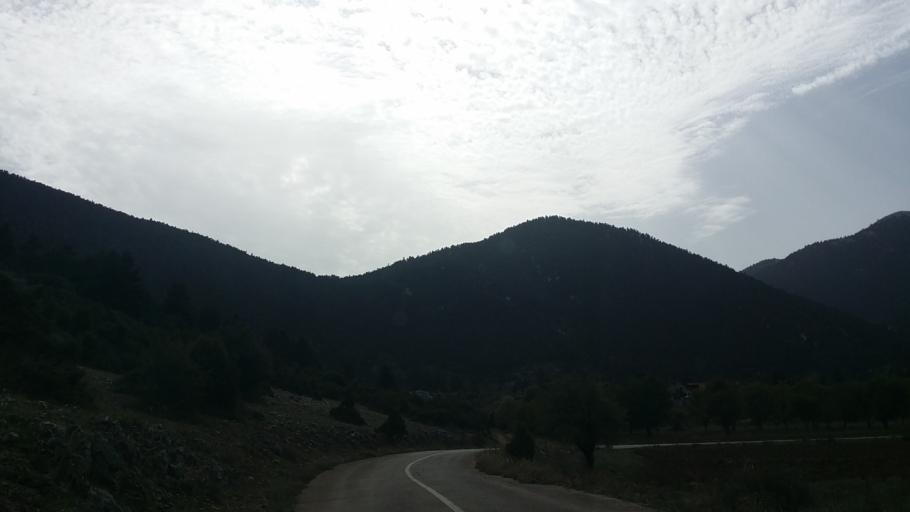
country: GR
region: Central Greece
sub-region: Nomos Voiotias
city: Kyriaki
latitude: 38.3718
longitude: 22.8473
